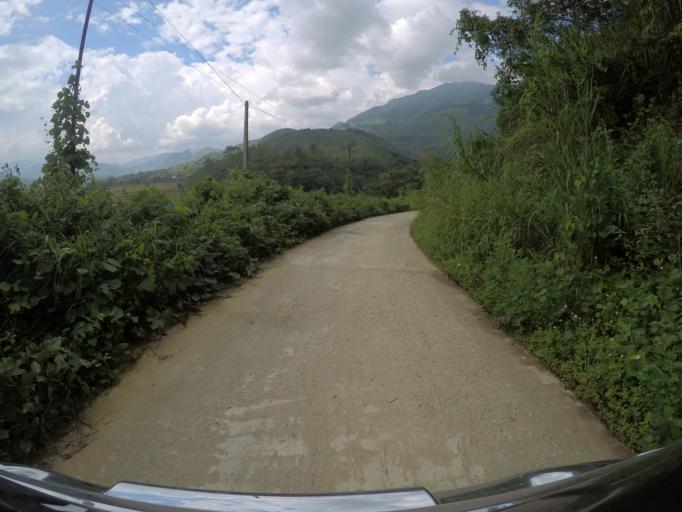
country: VN
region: Yen Bai
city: Son Thinh
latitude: 21.6610
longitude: 104.5106
